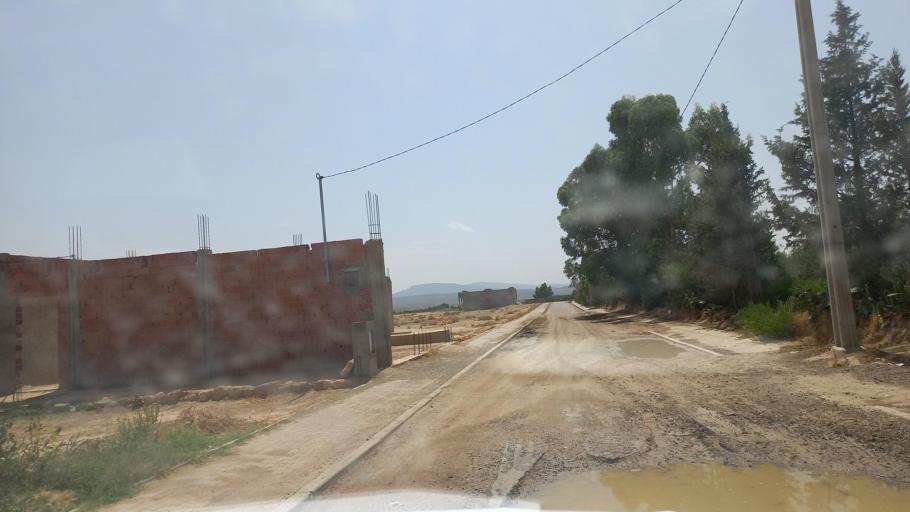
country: TN
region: Al Qasrayn
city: Kasserine
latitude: 35.2493
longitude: 9.0249
